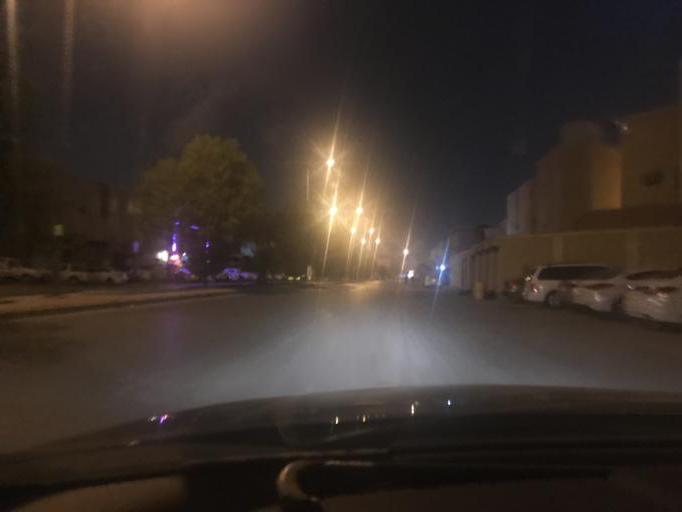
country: SA
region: Ar Riyad
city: Riyadh
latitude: 24.7592
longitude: 46.7613
